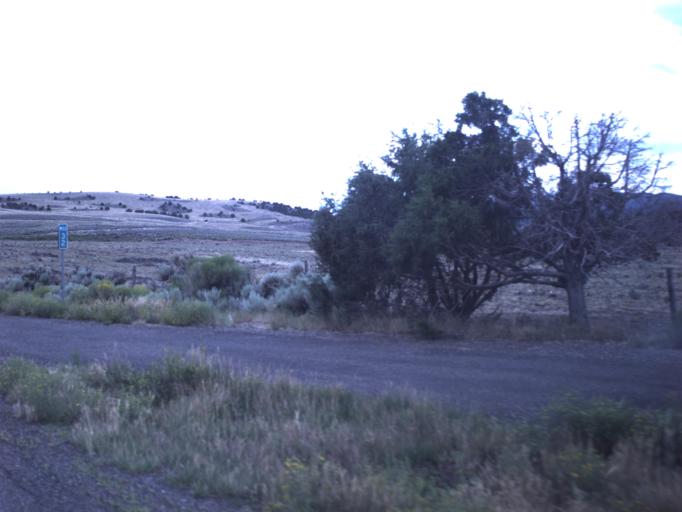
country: US
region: Utah
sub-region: Wayne County
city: Loa
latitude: 38.5731
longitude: -111.8415
